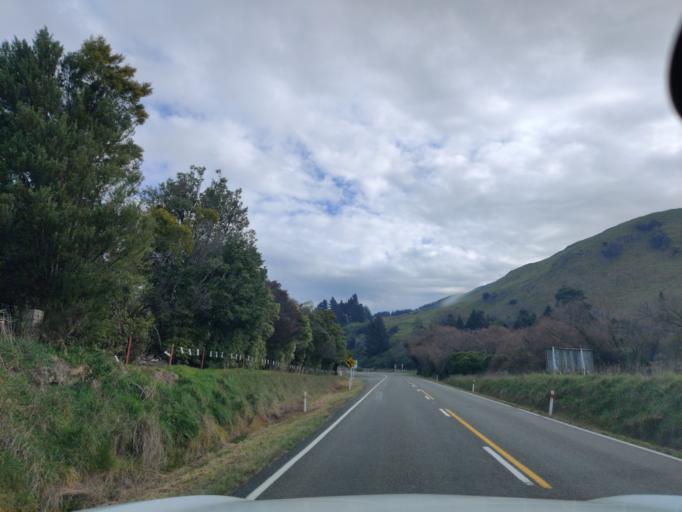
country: NZ
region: Manawatu-Wanganui
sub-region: Palmerston North City
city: Palmerston North
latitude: -40.3362
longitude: 175.8357
